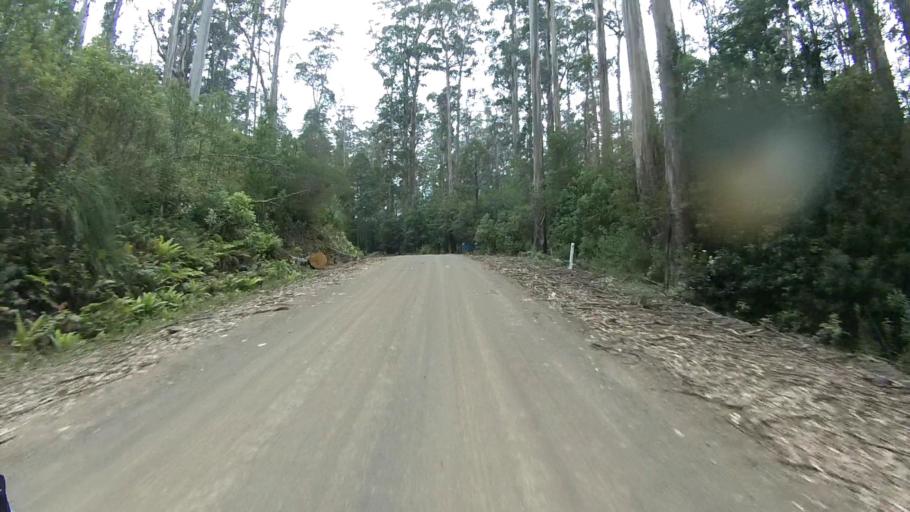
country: AU
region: Tasmania
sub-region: Sorell
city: Sorell
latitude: -42.7025
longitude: 147.8561
